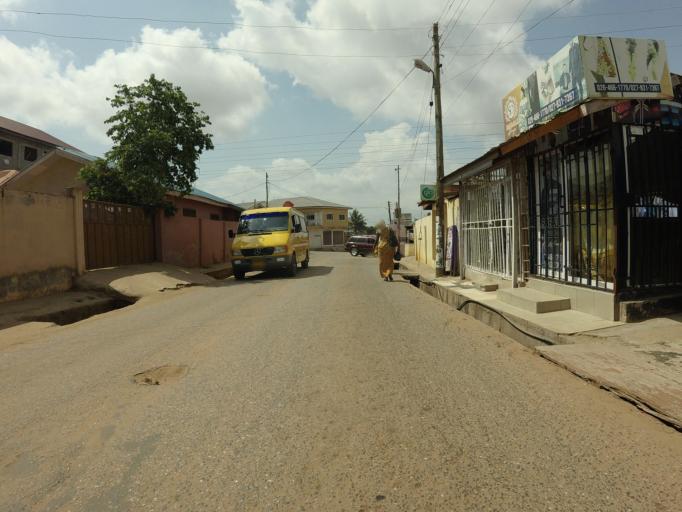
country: GH
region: Greater Accra
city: Dome
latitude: 5.6159
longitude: -0.2481
